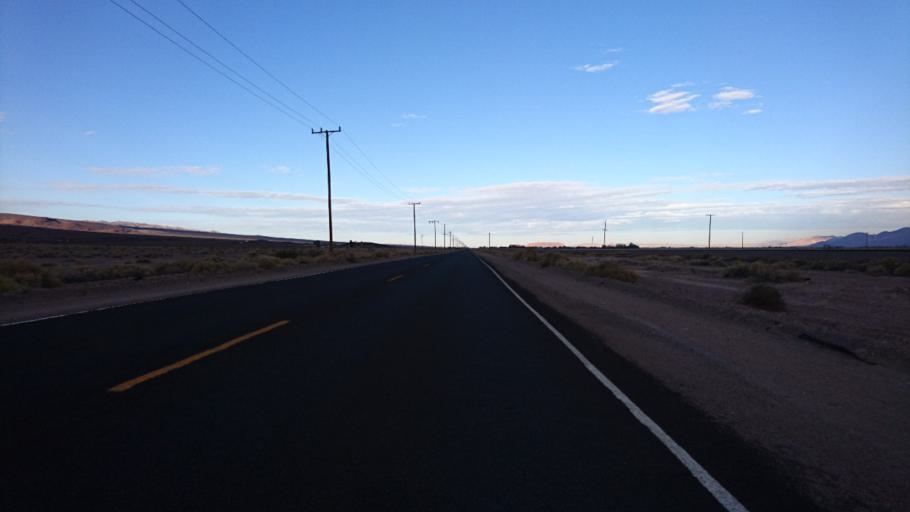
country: US
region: California
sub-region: San Bernardino County
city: Barstow
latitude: 34.8359
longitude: -116.7122
